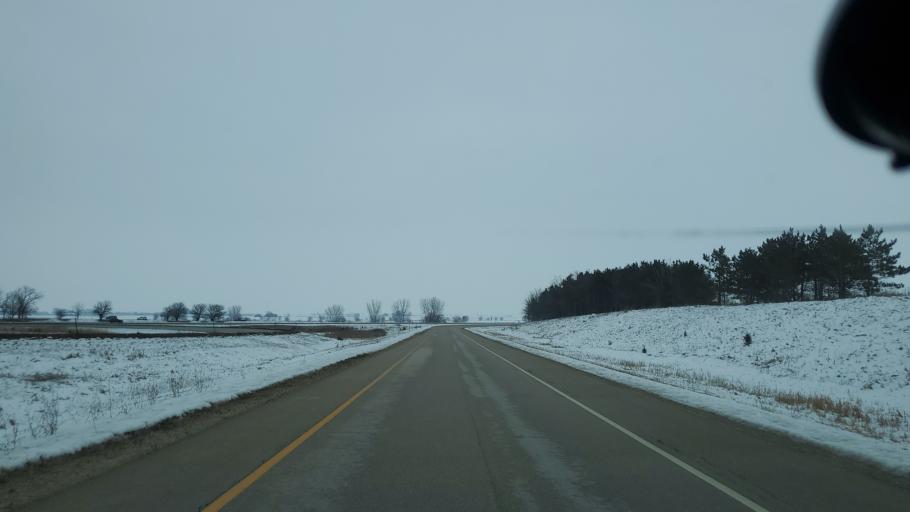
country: US
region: Illinois
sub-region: Ogle County
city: Rochelle
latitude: 41.9025
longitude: -89.0177
